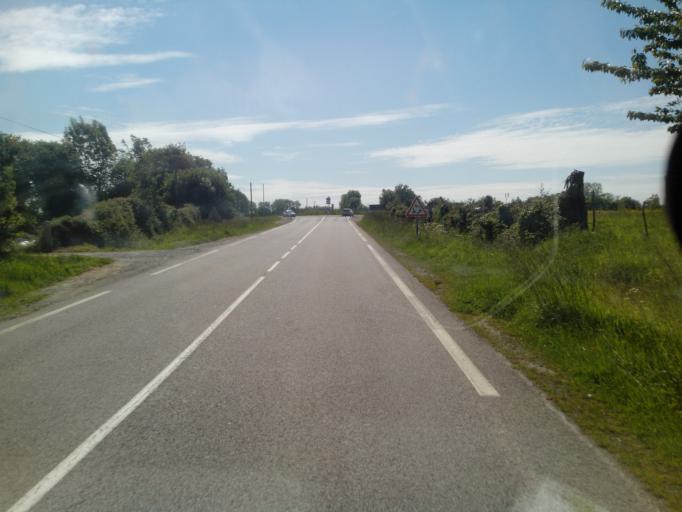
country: FR
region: Haute-Normandie
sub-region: Departement de l'Eure
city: Beuzeville
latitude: 49.3320
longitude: 0.3151
